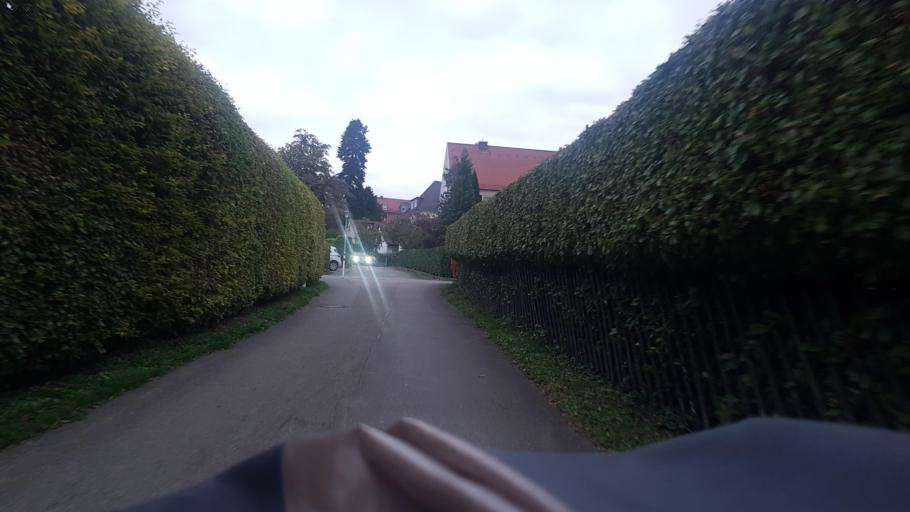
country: DE
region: Bavaria
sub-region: Swabia
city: Lindau
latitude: 47.5538
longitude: 9.6867
